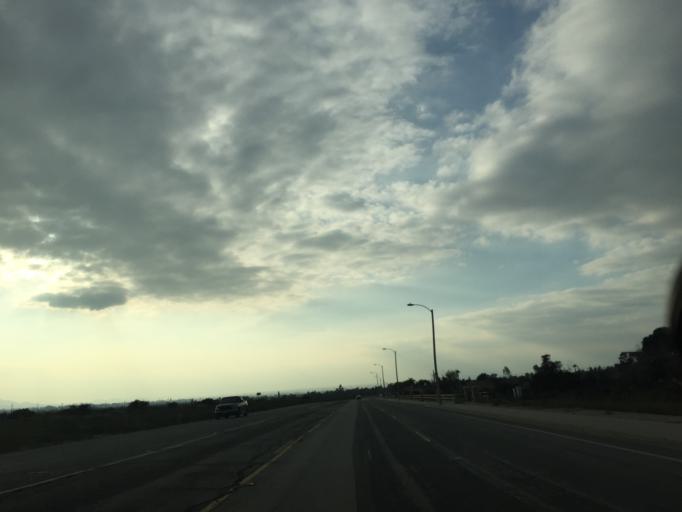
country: US
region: California
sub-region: San Bernardino County
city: Mentone
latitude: 34.1099
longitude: -117.1542
